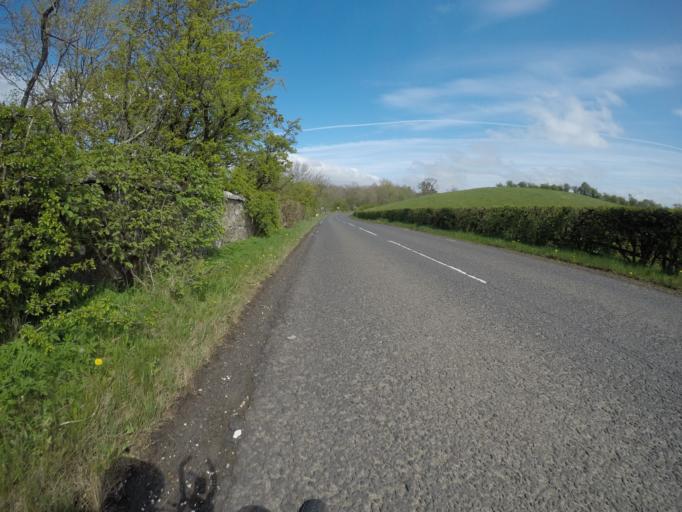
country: GB
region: Scotland
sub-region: East Ayrshire
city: Stewarton
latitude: 55.6702
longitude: -4.5305
